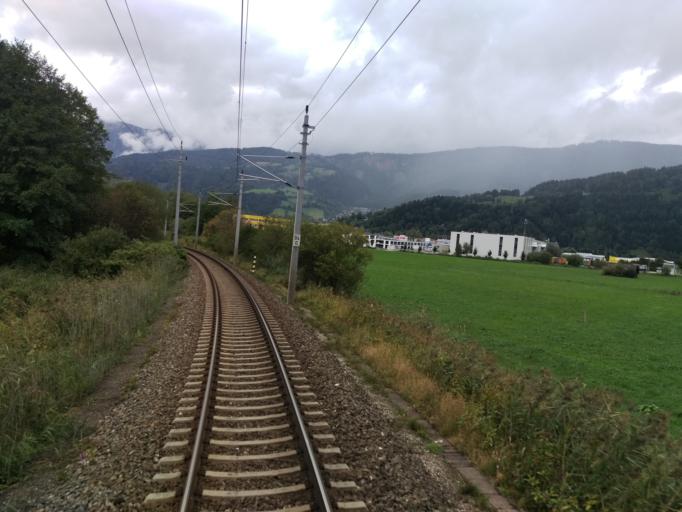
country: AT
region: Styria
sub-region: Politischer Bezirk Liezen
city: Liezen
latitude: 47.5554
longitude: 14.2559
